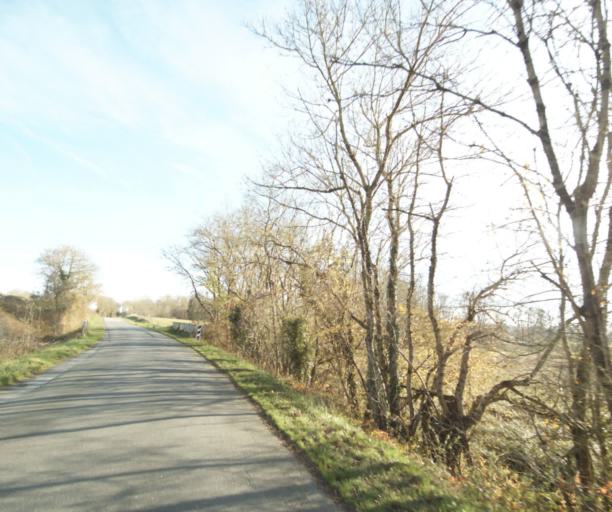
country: FR
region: Poitou-Charentes
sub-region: Departement de la Charente-Maritime
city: Chaniers
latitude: 45.7155
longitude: -0.5525
